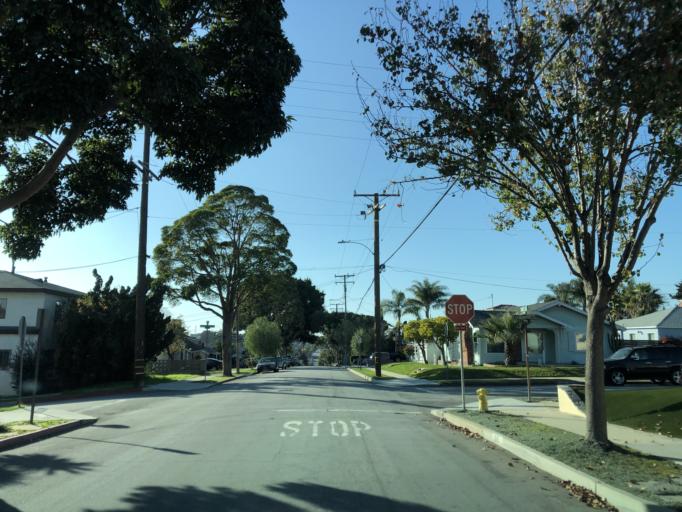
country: US
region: California
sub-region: Los Angeles County
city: El Segundo
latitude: 33.9270
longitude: -118.4133
